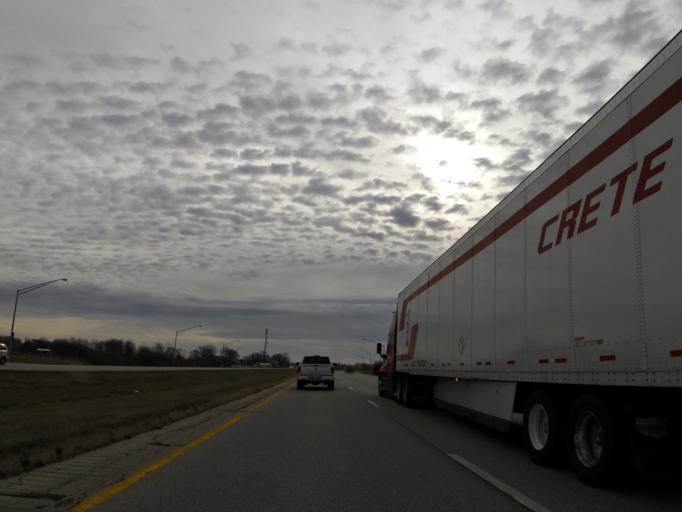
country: US
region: Indiana
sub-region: Hendricks County
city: Pittsboro
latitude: 39.9042
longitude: -86.5591
